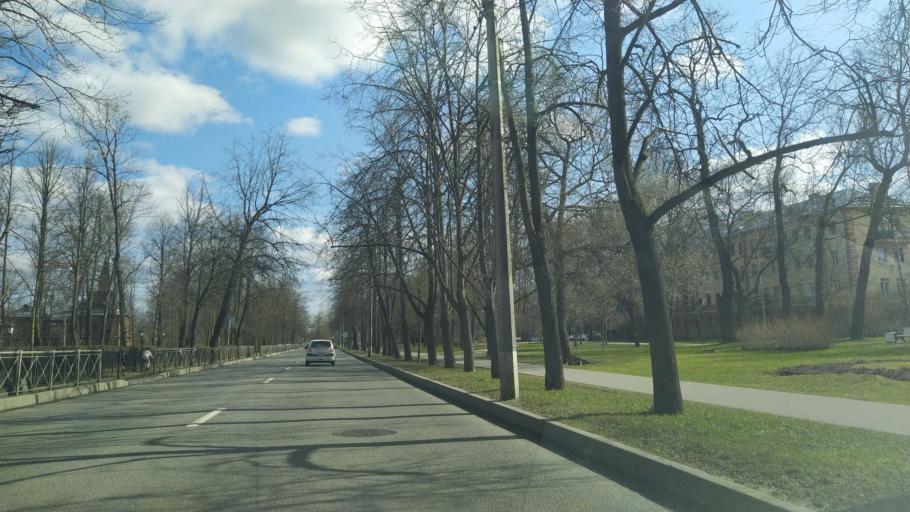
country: RU
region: St.-Petersburg
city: Pushkin
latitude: 59.7058
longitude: 30.4174
